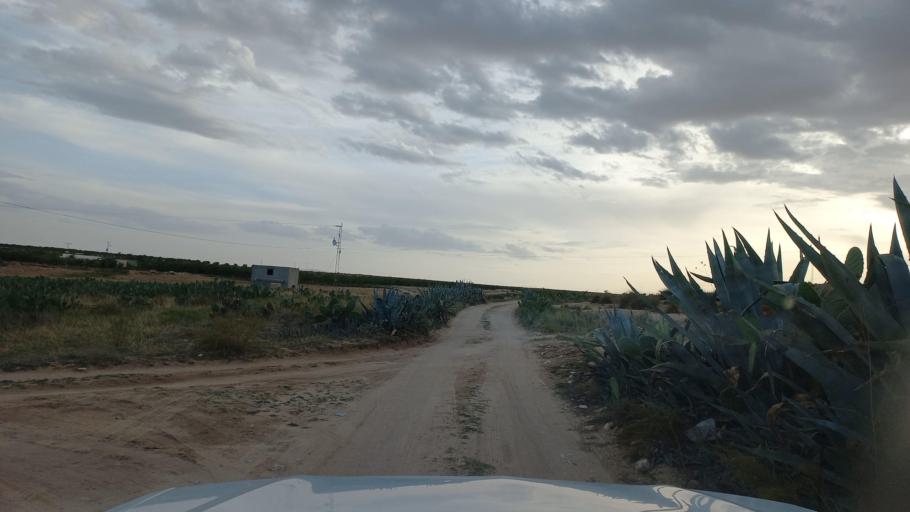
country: TN
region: Al Qasrayn
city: Sbiba
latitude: 35.4254
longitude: 9.0958
